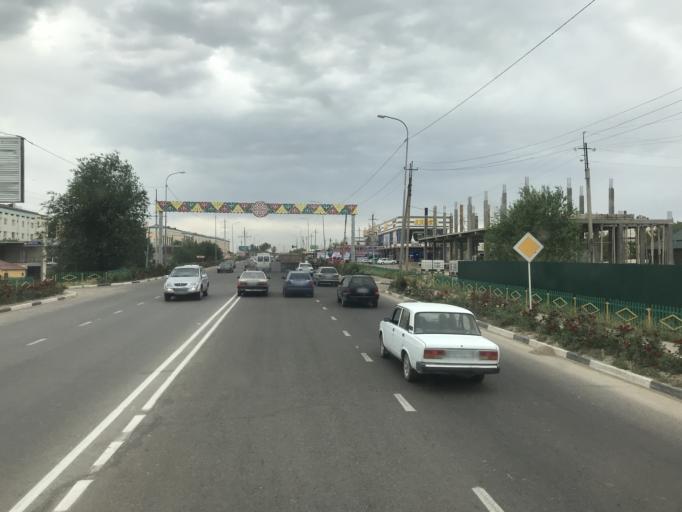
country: KZ
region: Ongtustik Qazaqstan
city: Saryaghash
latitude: 41.4667
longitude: 69.1685
